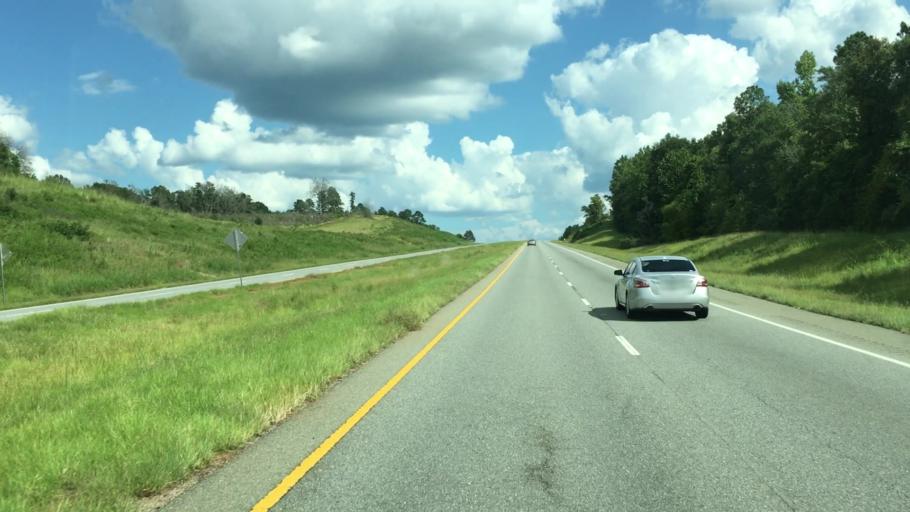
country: US
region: Georgia
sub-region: Wilkinson County
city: Irwinton
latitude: 32.7115
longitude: -83.1372
